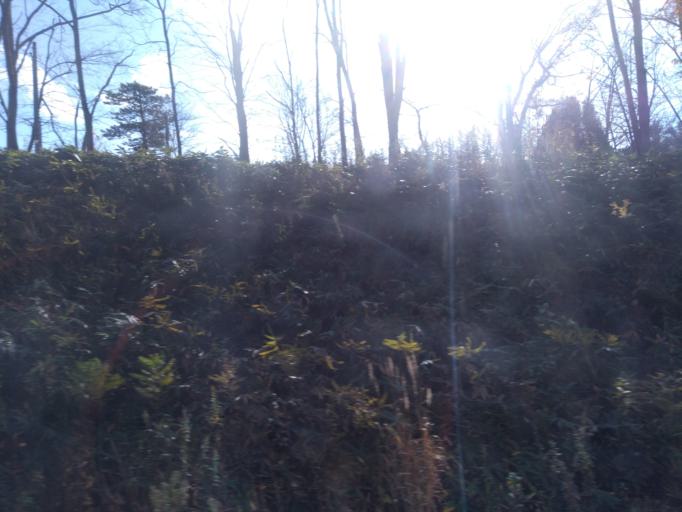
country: JP
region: Hokkaido
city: Kitahiroshima
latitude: 42.9945
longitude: 141.5462
